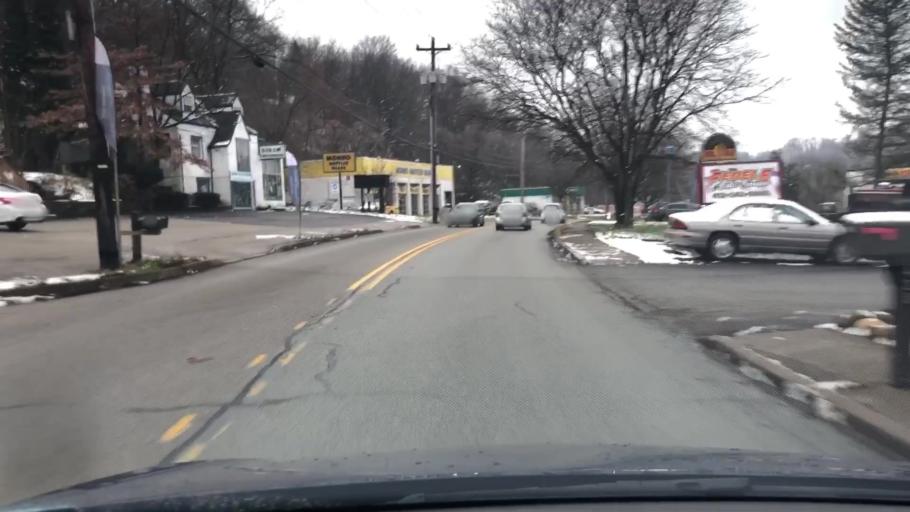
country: US
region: Pennsylvania
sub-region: Allegheny County
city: Churchill
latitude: 40.4548
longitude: -79.8232
